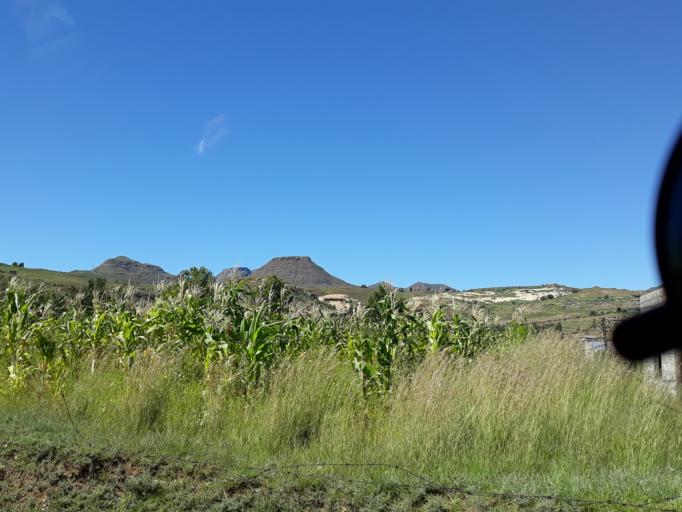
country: LS
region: Mohale's Hoek District
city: Mohale's Hoek
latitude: -30.1087
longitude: 27.4762
